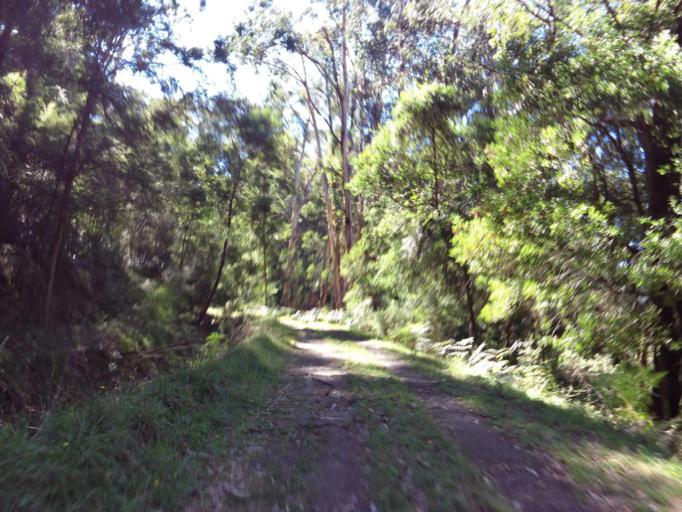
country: AU
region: Victoria
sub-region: Yarra Ranges
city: Launching Place
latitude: -37.7408
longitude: 145.5788
